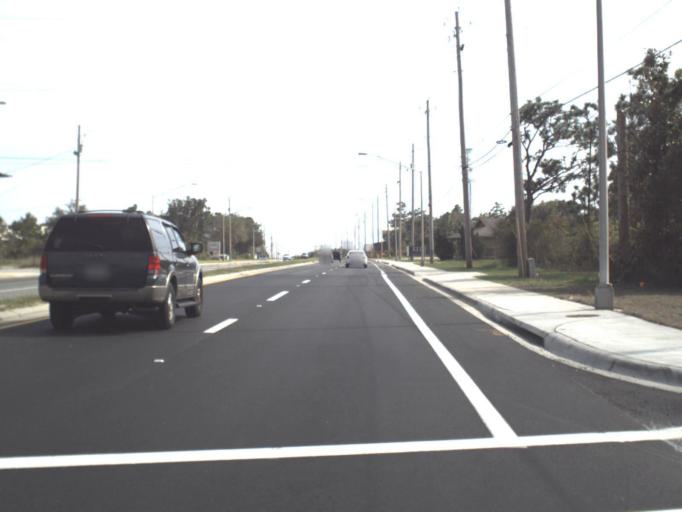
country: US
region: Florida
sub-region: Santa Rosa County
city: Navarre
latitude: 30.4097
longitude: -86.8704
